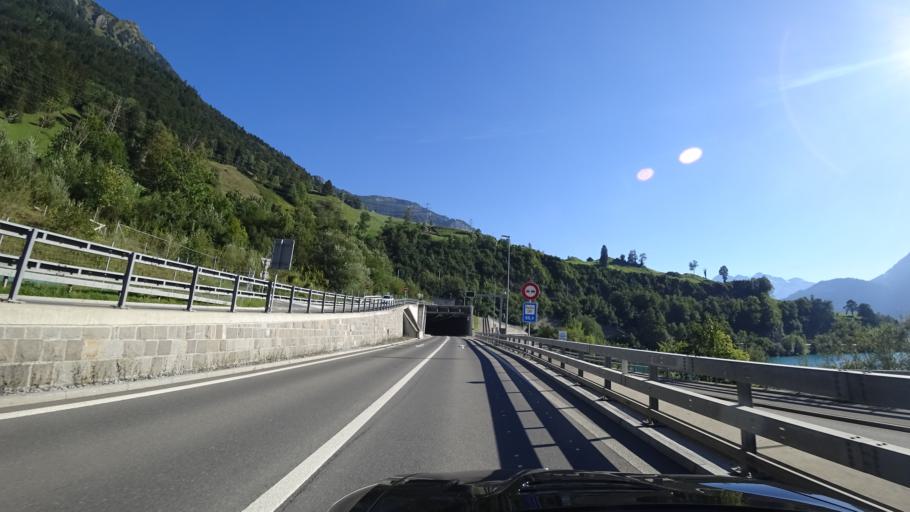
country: CH
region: Obwalden
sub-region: Obwalden
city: Lungern
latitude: 46.8029
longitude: 8.1696
